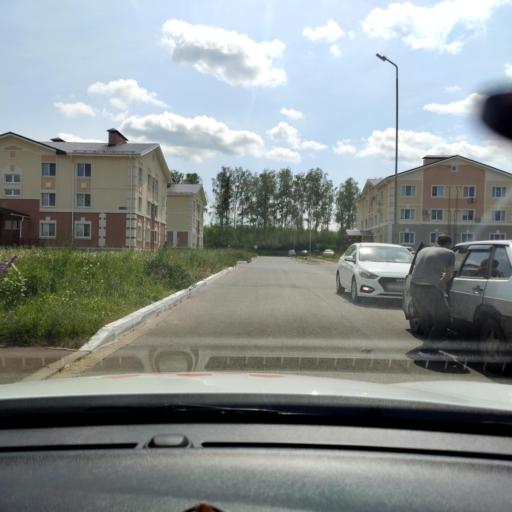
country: RU
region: Tatarstan
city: Stolbishchi
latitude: 55.7072
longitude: 49.3457
